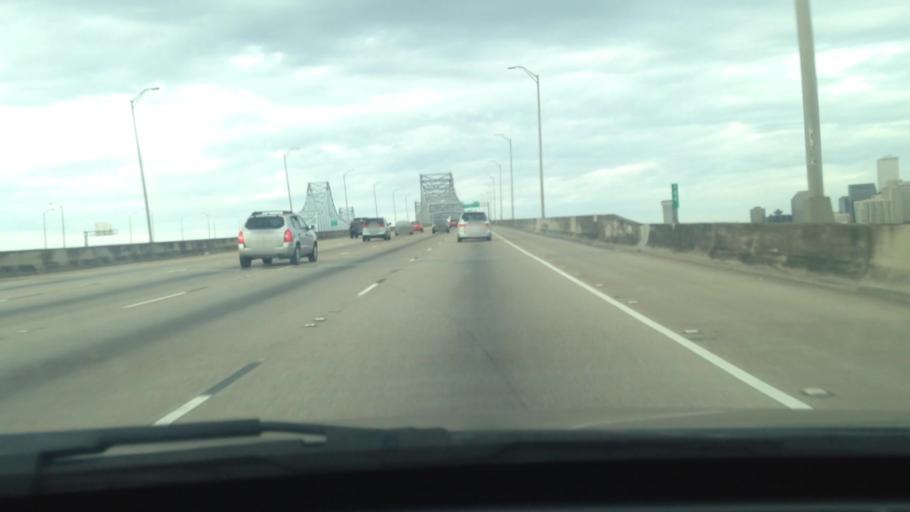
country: US
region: Louisiana
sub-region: Jefferson Parish
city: Gretna
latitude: 29.9386
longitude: -90.0437
